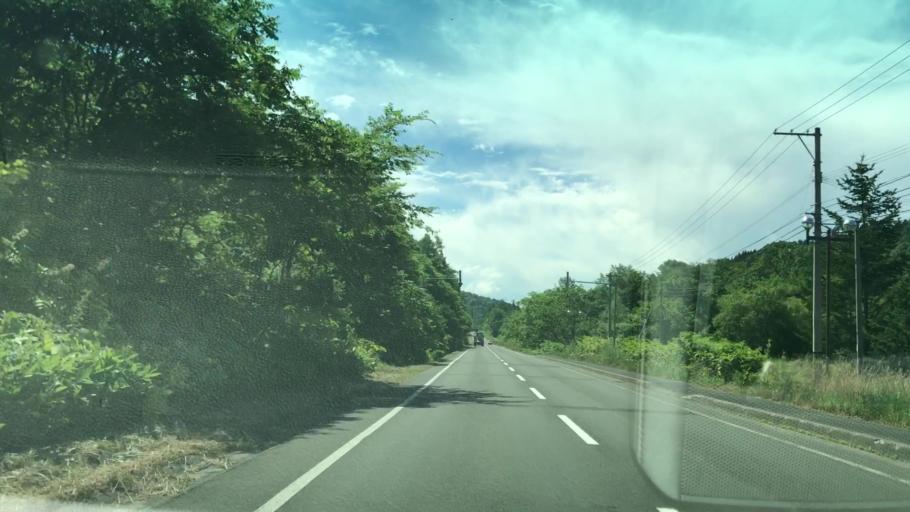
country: JP
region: Hokkaido
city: Shimo-furano
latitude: 42.9477
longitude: 142.4430
